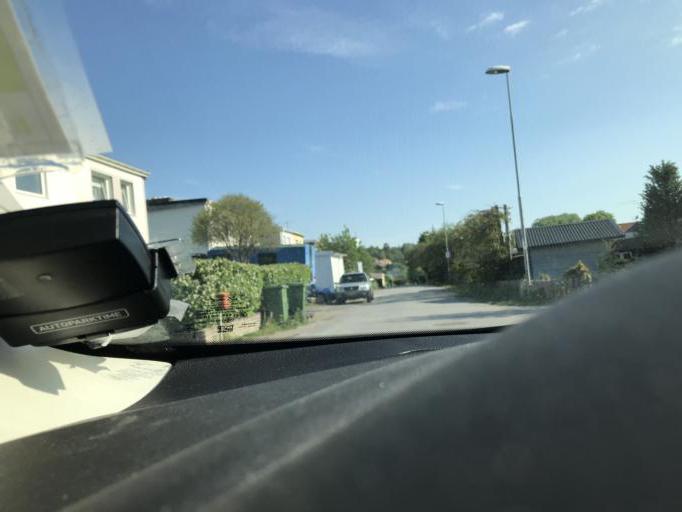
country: SE
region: Stockholm
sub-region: Botkyrka Kommun
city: Tumba
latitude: 59.1883
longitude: 17.8169
